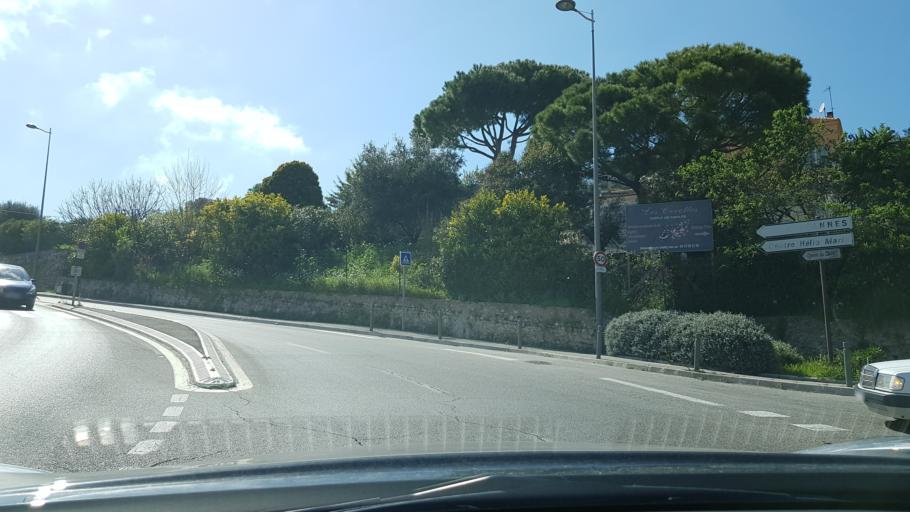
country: FR
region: Provence-Alpes-Cote d'Azur
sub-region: Departement des Alpes-Maritimes
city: Vallauris
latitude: 43.5794
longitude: 7.0491
